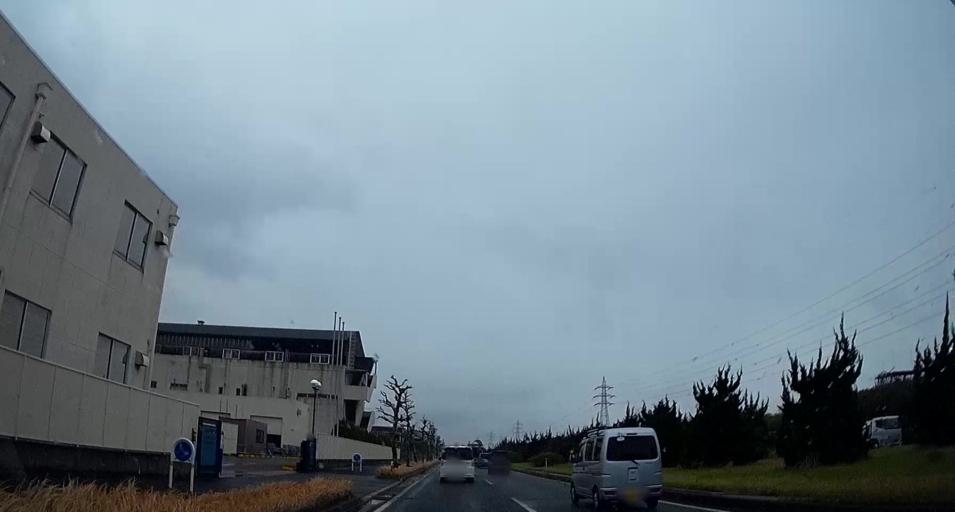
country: JP
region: Chiba
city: Ichihara
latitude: 35.5172
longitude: 140.0599
